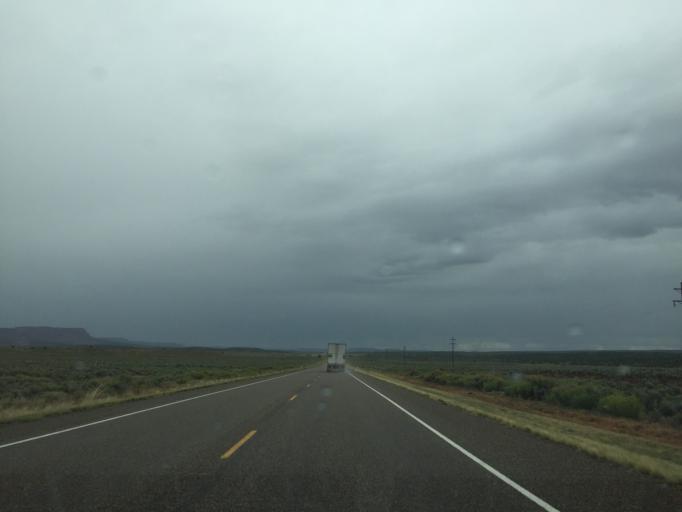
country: US
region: Utah
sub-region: Kane County
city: Kanab
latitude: 37.1140
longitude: -112.1129
